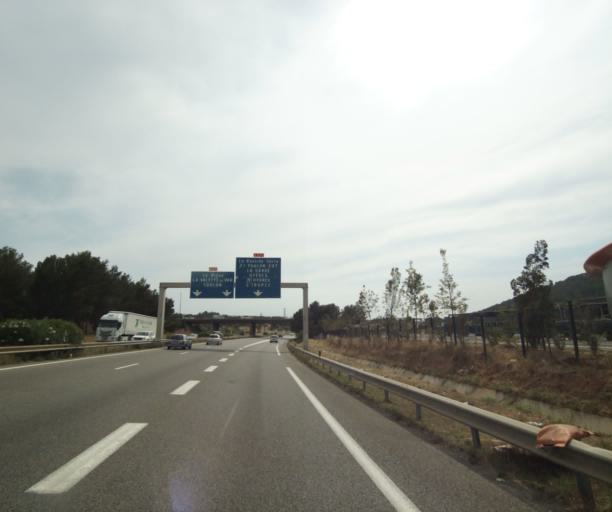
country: FR
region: Provence-Alpes-Cote d'Azur
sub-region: Departement du Var
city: La Farlede
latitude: 43.1461
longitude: 6.0311
